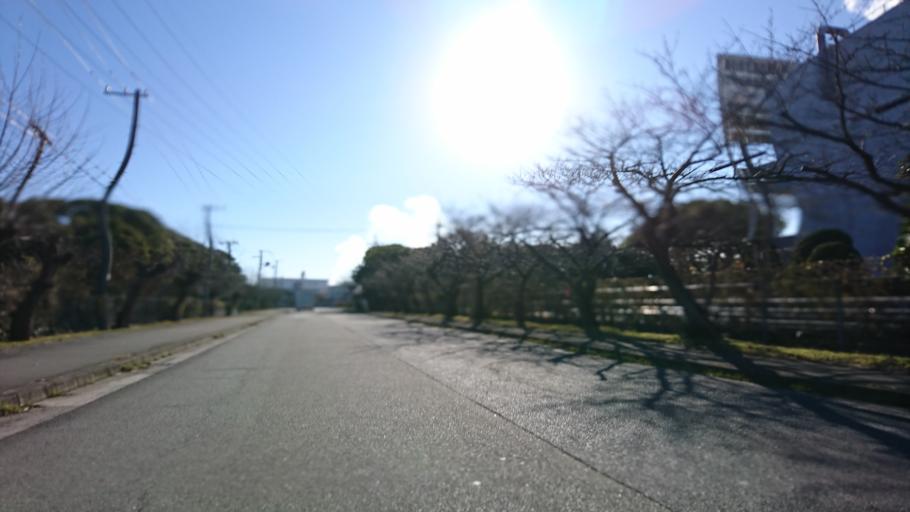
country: JP
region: Hyogo
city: Kakogawacho-honmachi
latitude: 34.7432
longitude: 134.7959
